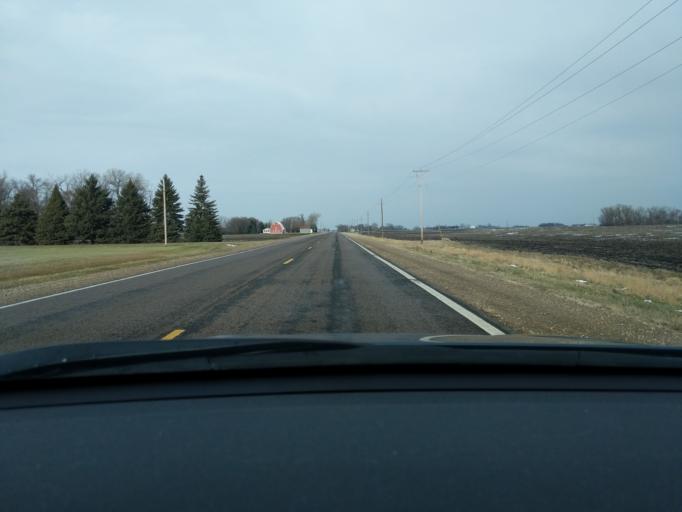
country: US
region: Minnesota
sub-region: Renville County
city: Renville
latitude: 44.7690
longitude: -95.3408
